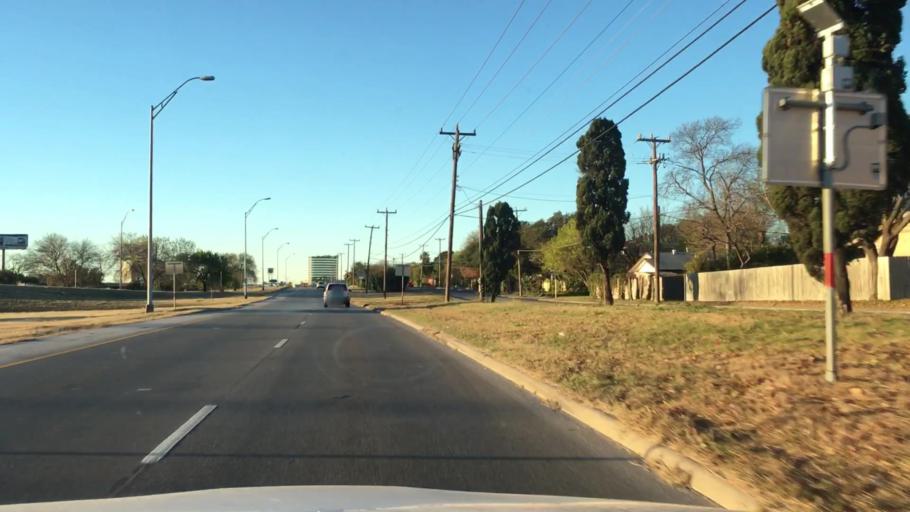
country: US
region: Texas
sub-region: Bexar County
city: Castle Hills
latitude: 29.5382
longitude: -98.4937
